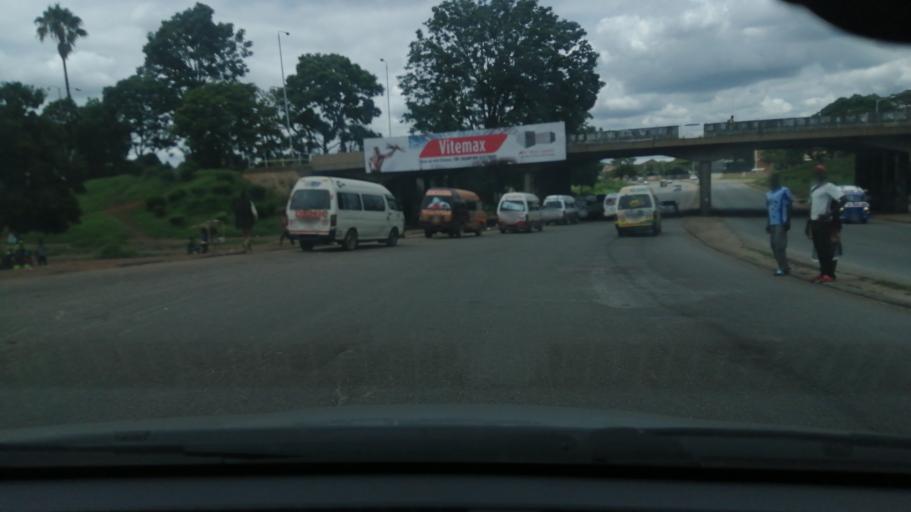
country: ZW
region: Harare
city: Harare
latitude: -17.8463
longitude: 31.0391
